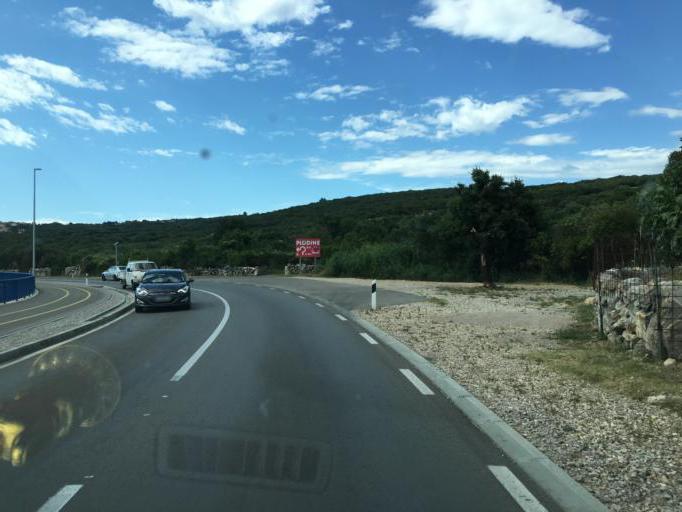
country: HR
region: Primorsko-Goranska
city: Punat
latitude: 45.0388
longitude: 14.6264
